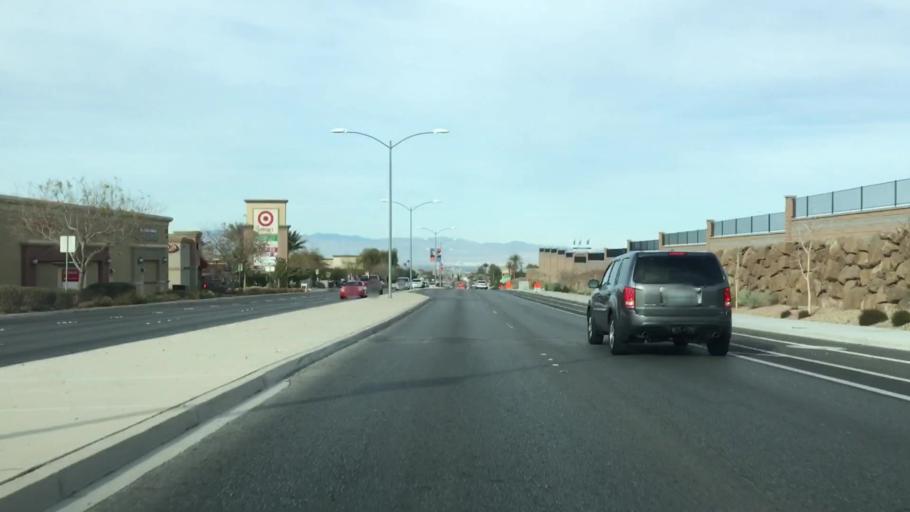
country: US
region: Nevada
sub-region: Clark County
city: Whitney
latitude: 36.0011
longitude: -115.0832
